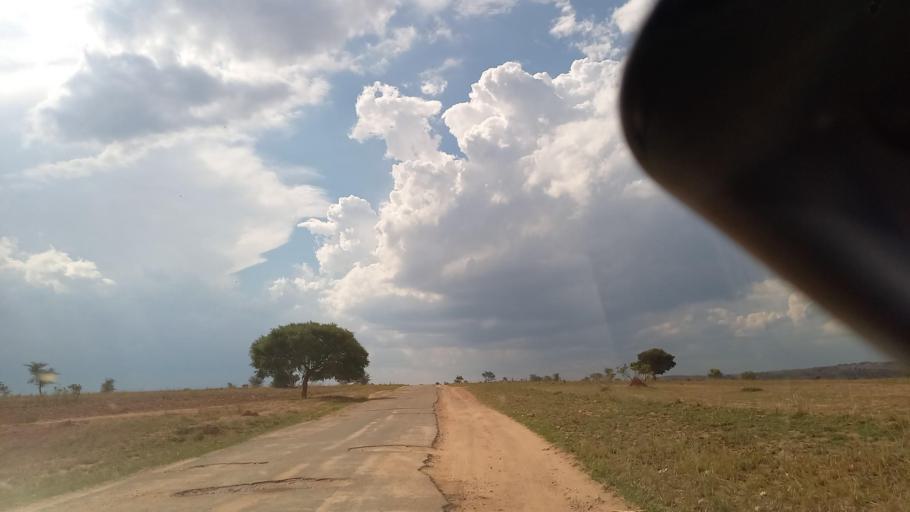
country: ZM
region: Lusaka
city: Kafue
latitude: -16.1998
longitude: 28.1055
